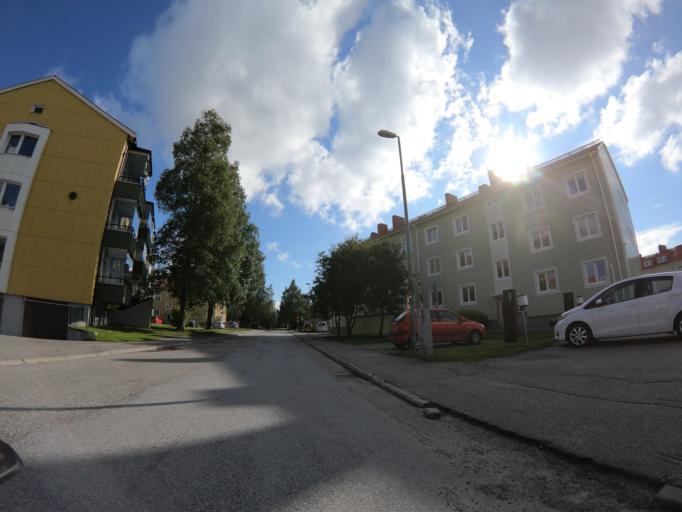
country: SE
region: Vaesterbotten
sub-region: Umea Kommun
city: Umea
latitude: 63.8333
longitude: 20.2765
